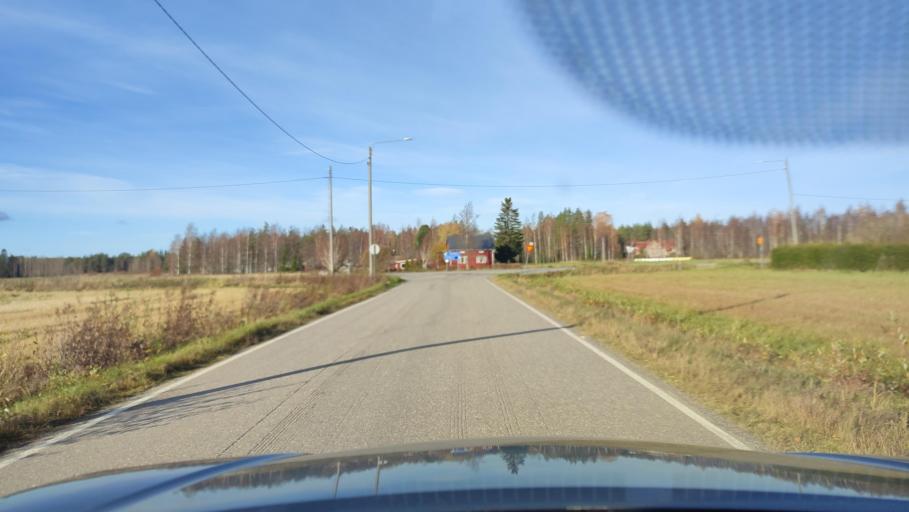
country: FI
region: Southern Ostrobothnia
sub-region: Suupohja
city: Teuva
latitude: 62.4511
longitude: 21.6017
